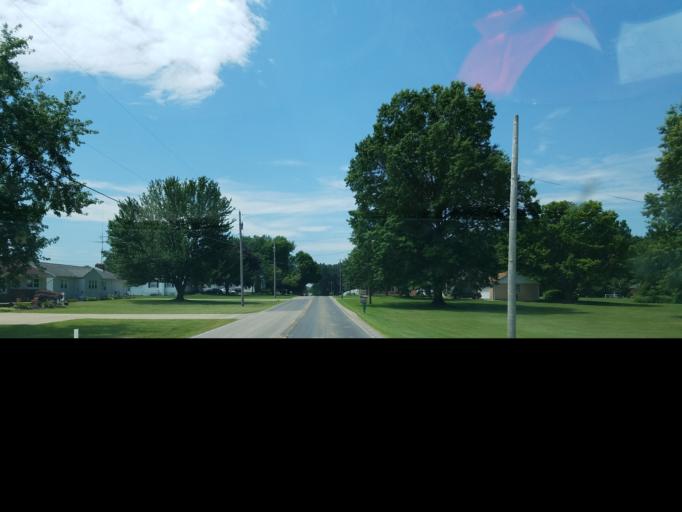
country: US
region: Ohio
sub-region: Ashland County
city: Ashland
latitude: 40.8657
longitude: -82.3559
